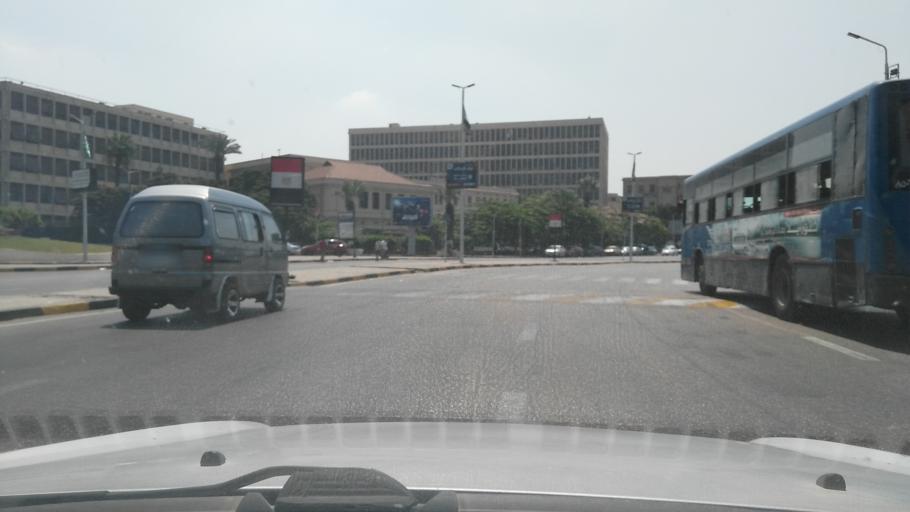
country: EG
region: Al Jizah
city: Al Jizah
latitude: 30.0280
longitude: 31.2107
